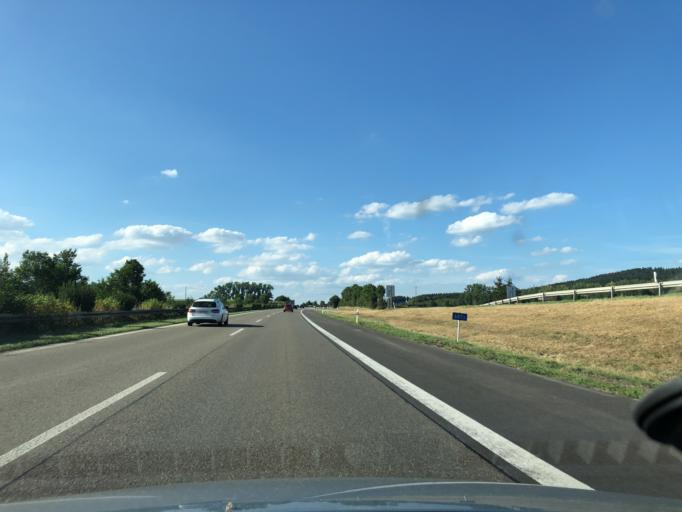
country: DE
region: Baden-Wuerttemberg
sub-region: Freiburg Region
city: Tuningen
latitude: 48.0001
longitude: 8.6055
